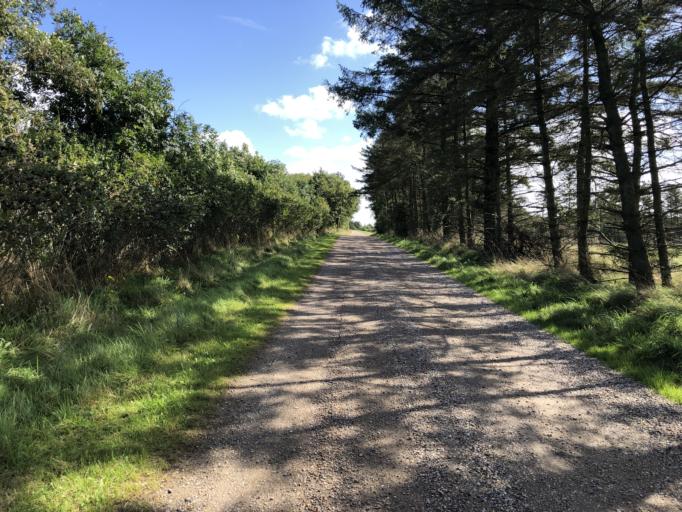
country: DK
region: Central Jutland
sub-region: Holstebro Kommune
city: Ulfborg
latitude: 56.3887
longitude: 8.3595
